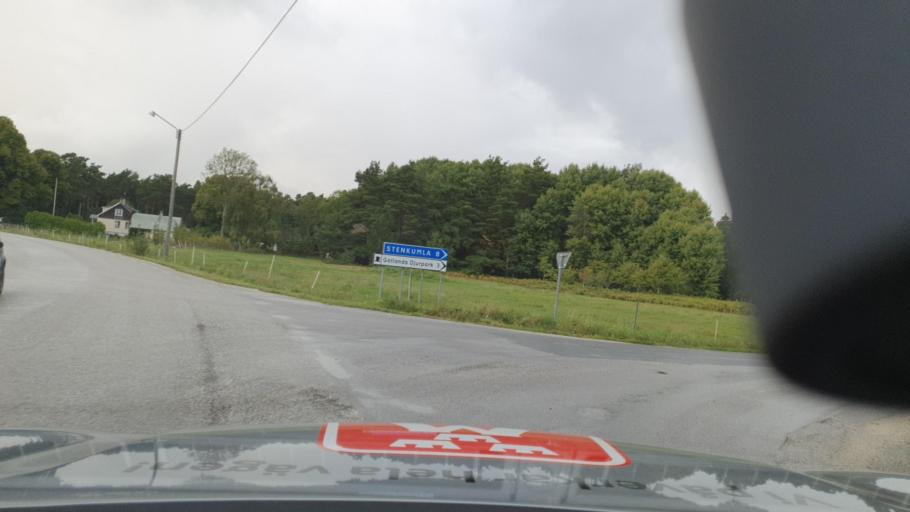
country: SE
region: Gotland
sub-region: Gotland
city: Klintehamn
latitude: 57.4947
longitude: 18.1967
